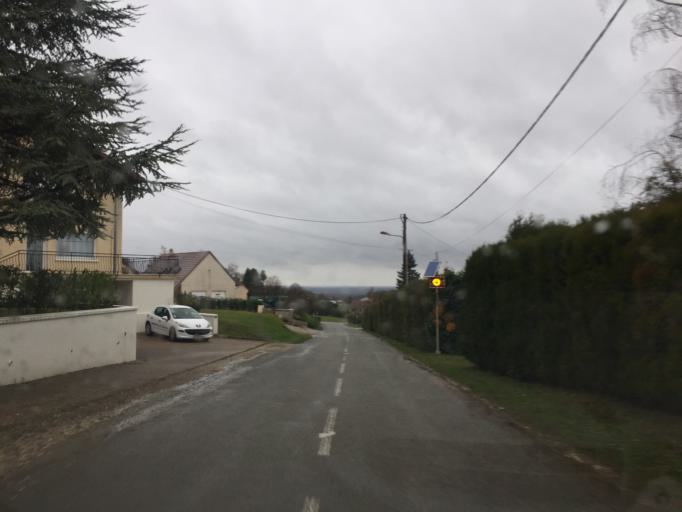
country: FR
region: Franche-Comte
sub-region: Departement du Jura
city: Dole
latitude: 47.1598
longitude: 5.5012
